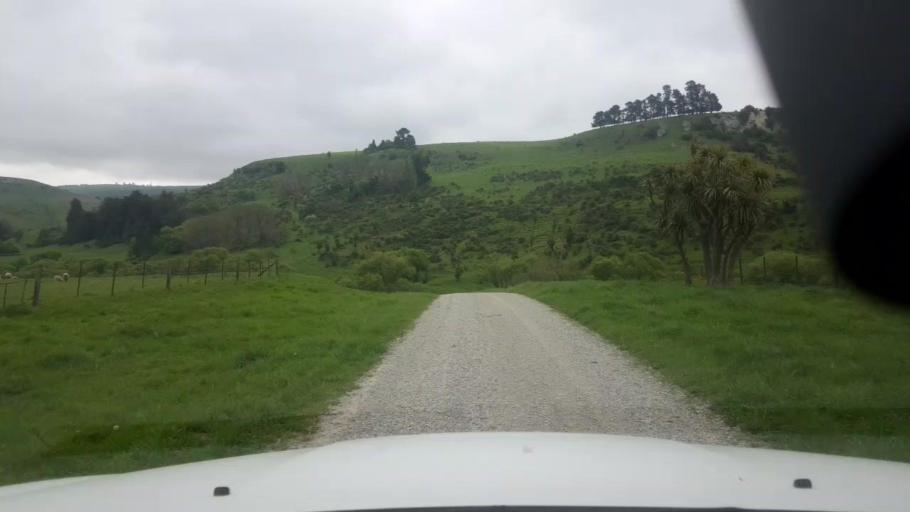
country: NZ
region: Canterbury
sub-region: Timaru District
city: Pleasant Point
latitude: -44.2250
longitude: 170.9631
